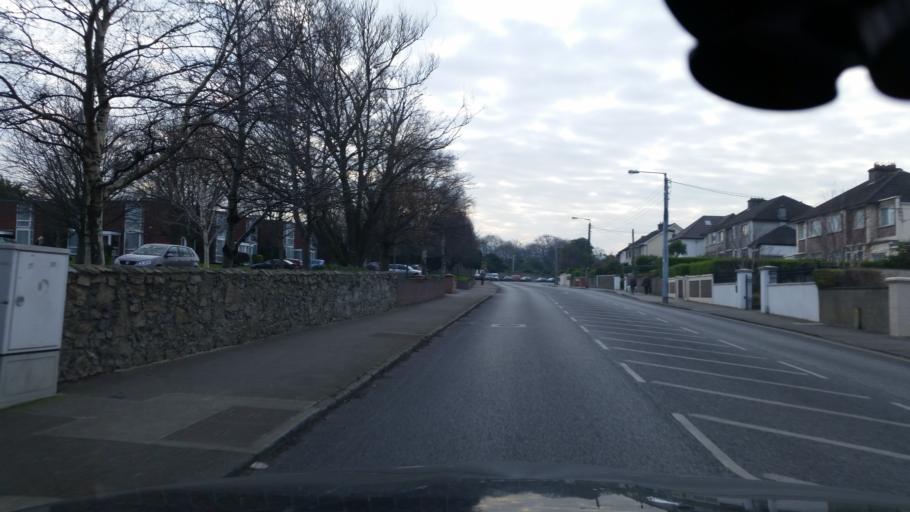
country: IE
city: Booterstown
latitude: 53.3022
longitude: -6.1998
